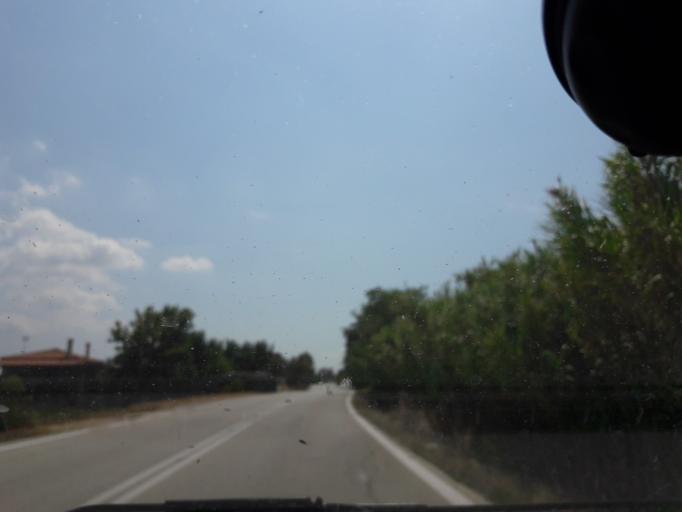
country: GR
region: North Aegean
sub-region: Nomos Lesvou
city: Myrina
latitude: 39.9320
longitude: 25.3404
